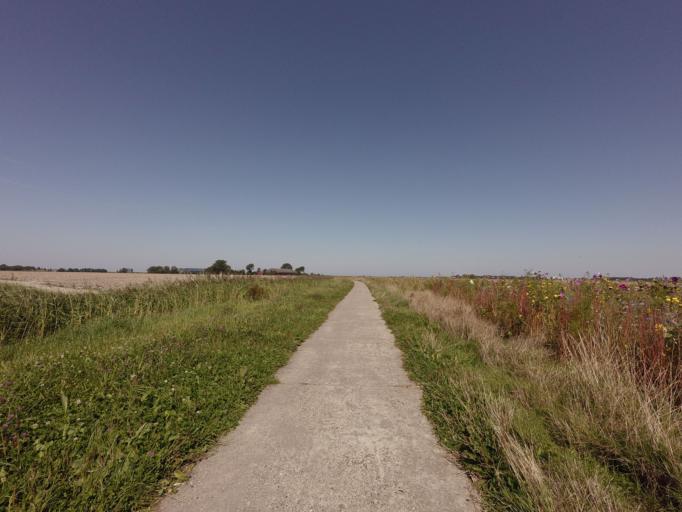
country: NL
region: Friesland
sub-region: Gemeente Dongeradeel
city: Anjum
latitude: 53.3884
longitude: 6.0661
